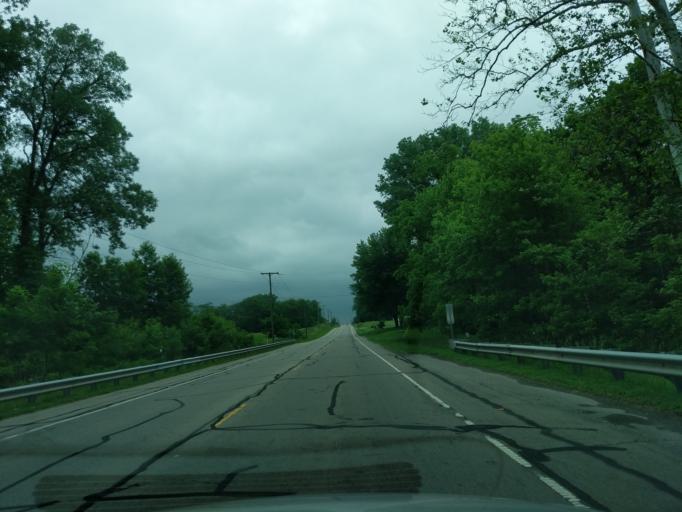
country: US
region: Indiana
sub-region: Madison County
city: Alexandria
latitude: 40.2778
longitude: -85.6422
